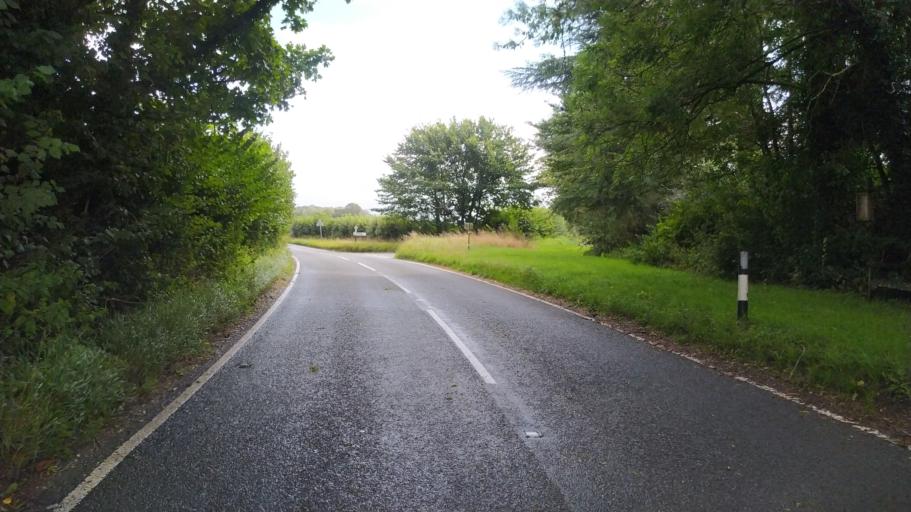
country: GB
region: England
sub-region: Wiltshire
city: Ansty
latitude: 50.9549
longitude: -2.0432
